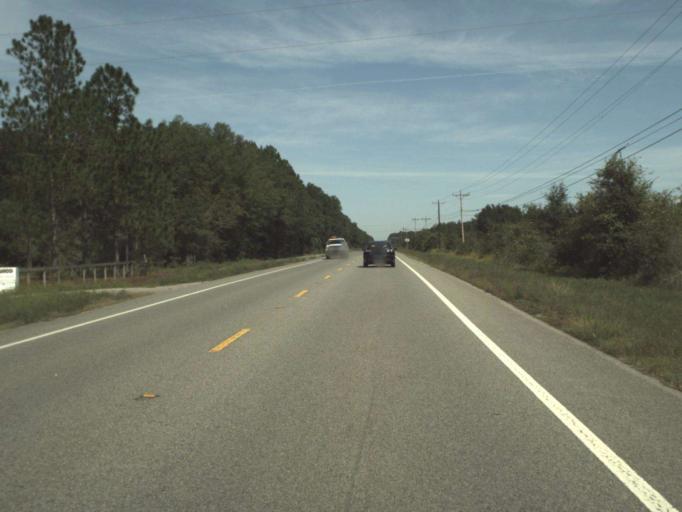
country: US
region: Florida
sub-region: Bay County
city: Lynn Haven
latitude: 30.4852
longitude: -85.6634
